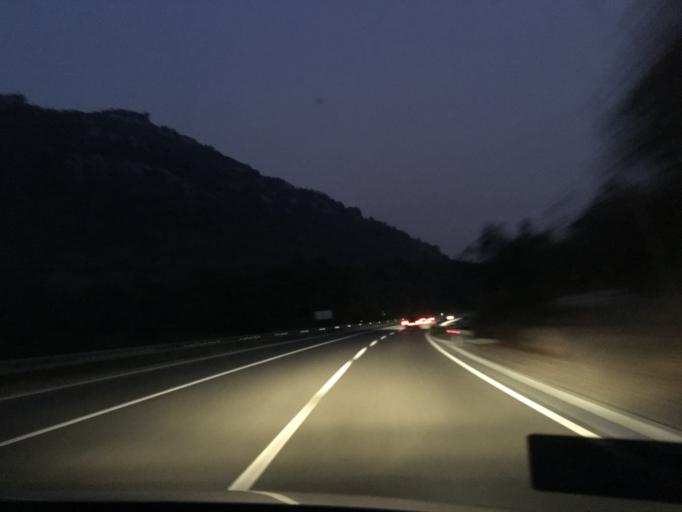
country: ME
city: Mojanovici
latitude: 42.3871
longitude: 19.0715
